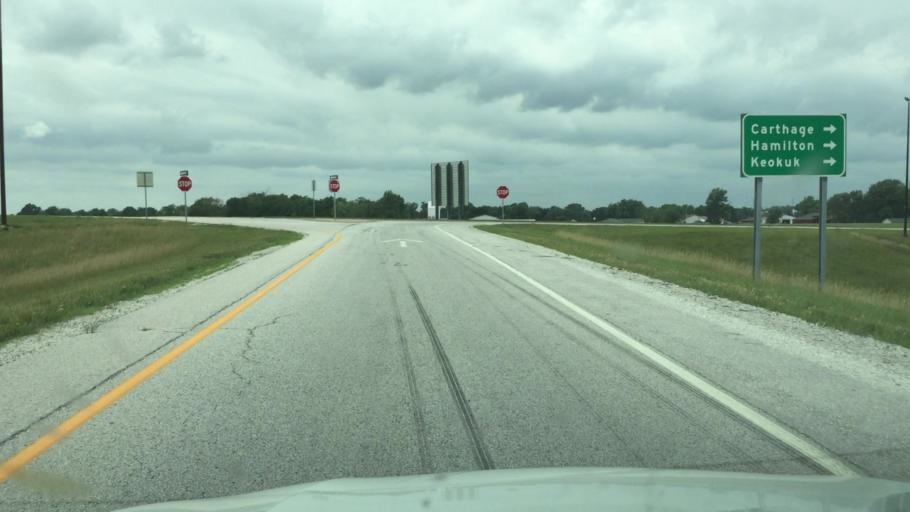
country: US
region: Illinois
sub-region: Hancock County
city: Carthage
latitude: 40.4139
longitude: -91.1131
